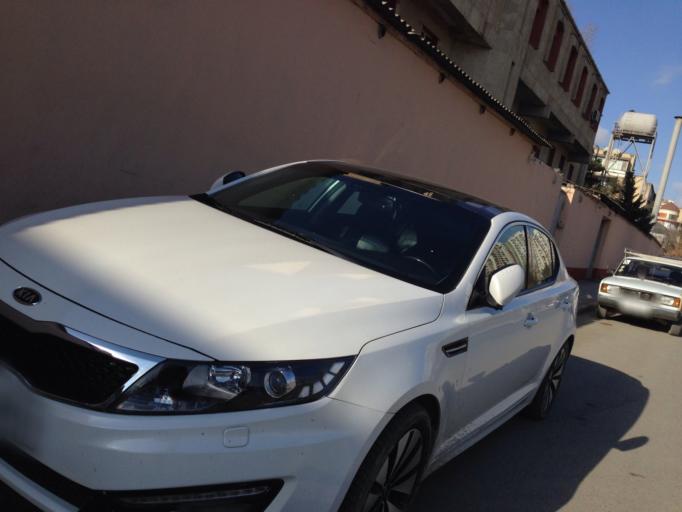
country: AZ
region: Baki
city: Baku
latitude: 40.4033
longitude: 49.8778
